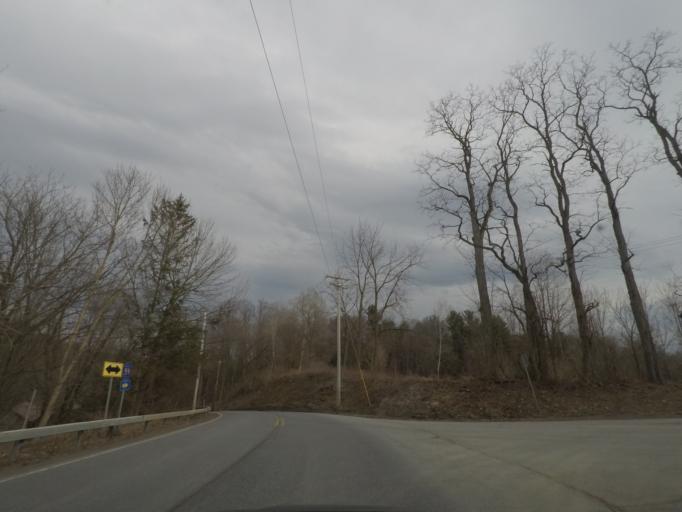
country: US
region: New York
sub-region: Washington County
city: Cambridge
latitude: 42.9579
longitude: -73.4540
